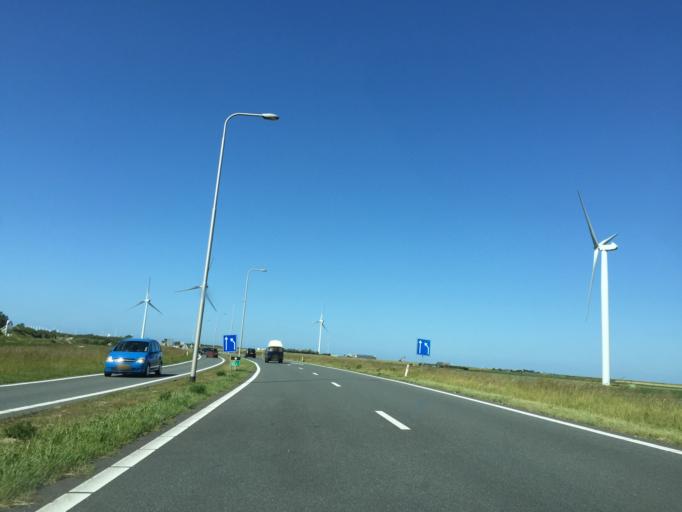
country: NL
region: Zeeland
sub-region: Gemeente Noord-Beveland
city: Kamperland
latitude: 51.5901
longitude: 3.6769
